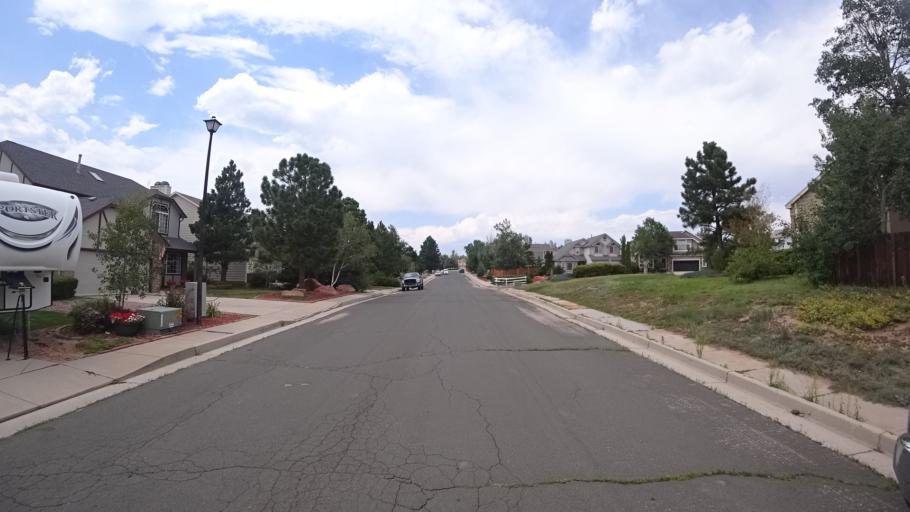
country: US
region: Colorado
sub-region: El Paso County
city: Black Forest
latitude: 38.9579
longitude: -104.7401
